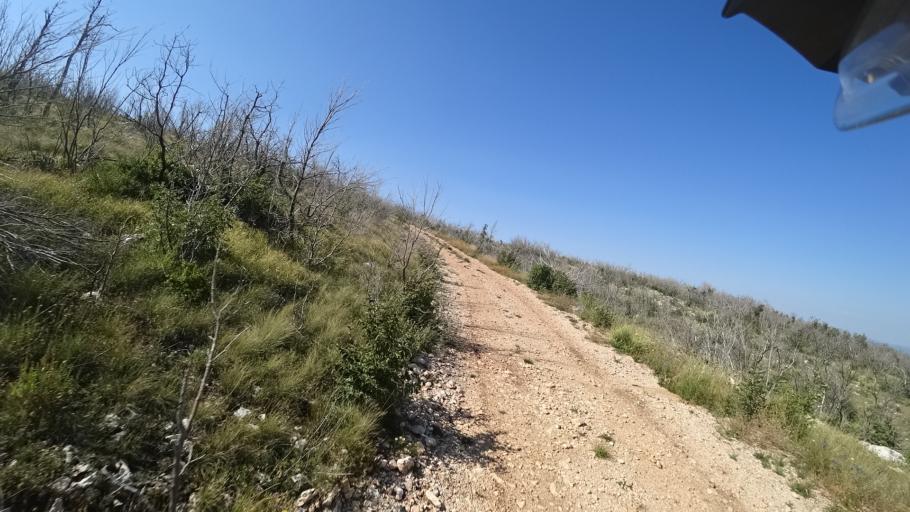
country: HR
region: Sibensko-Kniniska
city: Drnis
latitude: 43.9451
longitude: 16.1525
